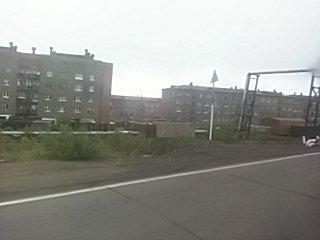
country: RU
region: Krasnoyarskiy
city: Dudinka
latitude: 69.4109
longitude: 86.1768
